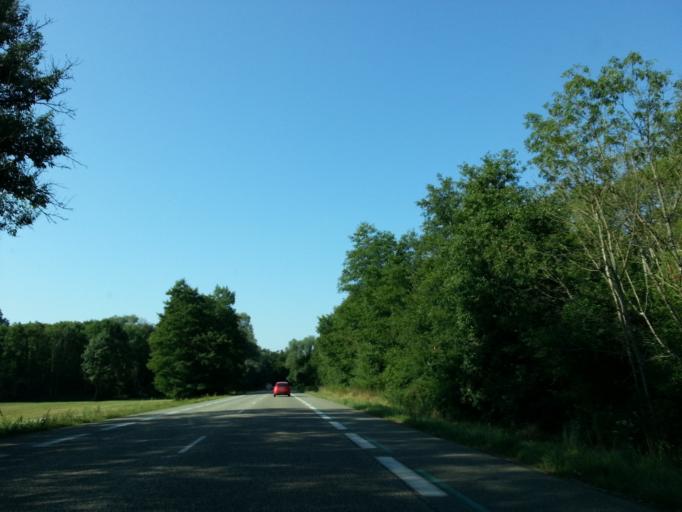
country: FR
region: Alsace
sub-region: Departement du Bas-Rhin
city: Surbourg
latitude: 48.9004
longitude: 7.8401
